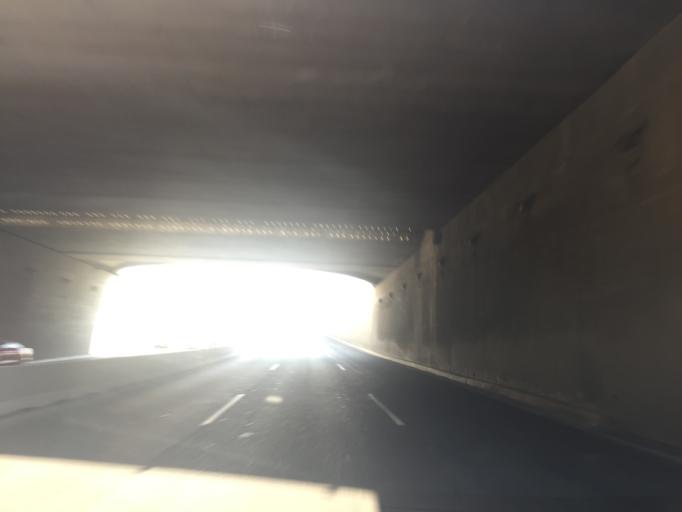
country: MX
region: Nuevo Leon
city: Guadalupe
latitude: 25.6527
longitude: -100.2770
